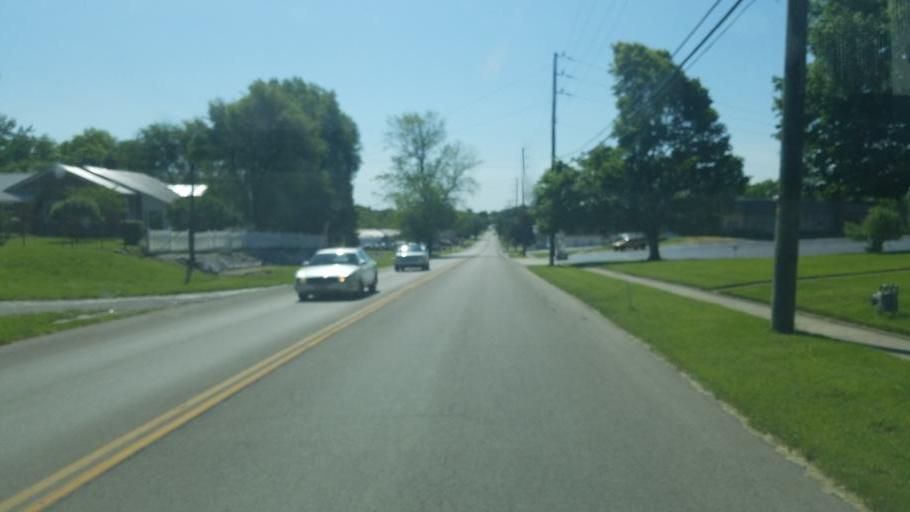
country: US
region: Ohio
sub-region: Hardin County
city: Kenton
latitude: 40.6503
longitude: -83.6211
